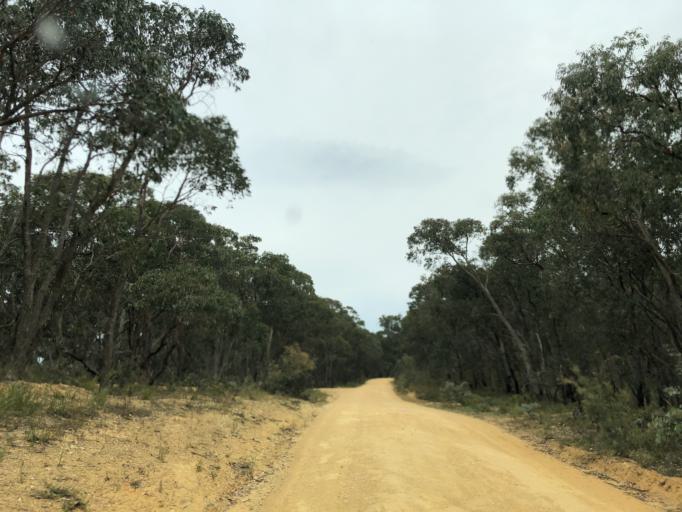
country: AU
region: Victoria
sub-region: Moorabool
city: Bacchus Marsh
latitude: -37.4975
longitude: 144.3522
